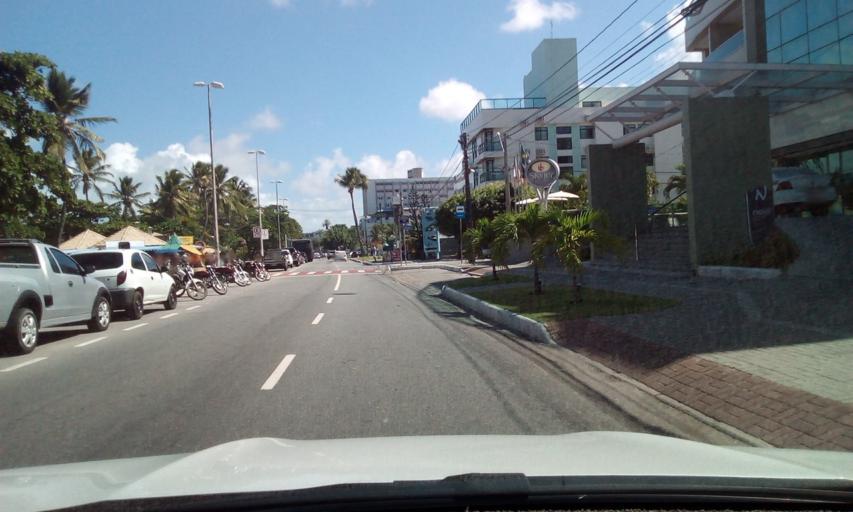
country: BR
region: Paraiba
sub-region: Joao Pessoa
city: Joao Pessoa
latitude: -7.1269
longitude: -34.8235
